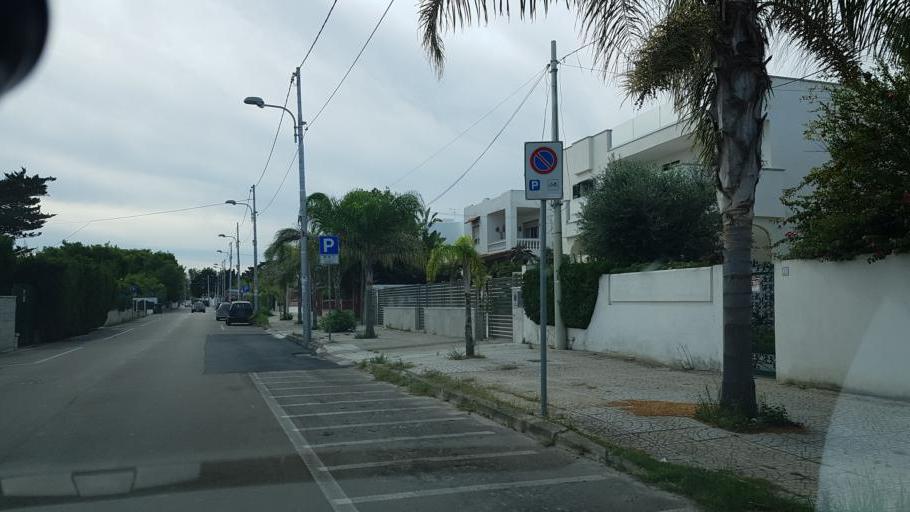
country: IT
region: Apulia
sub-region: Provincia di Lecce
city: Borgagne
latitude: 40.2722
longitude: 18.4284
